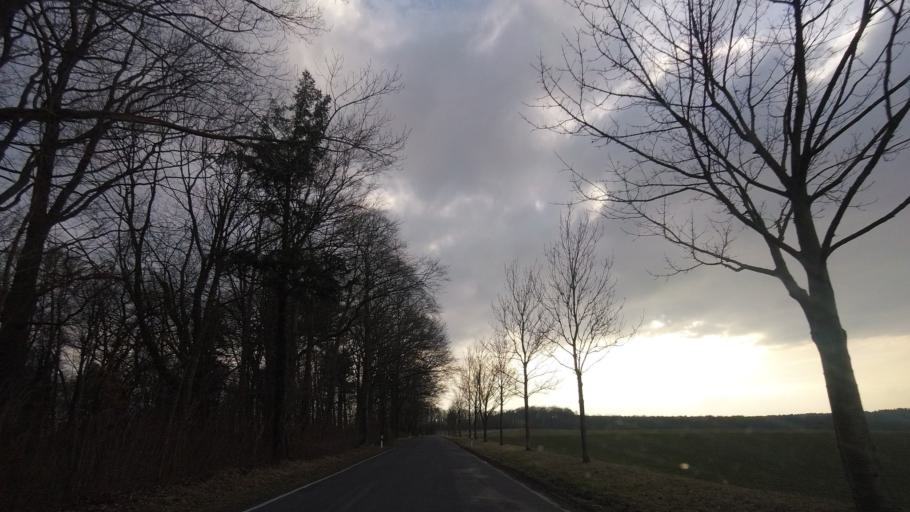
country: DE
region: Brandenburg
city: Belzig
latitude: 52.1545
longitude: 12.5263
